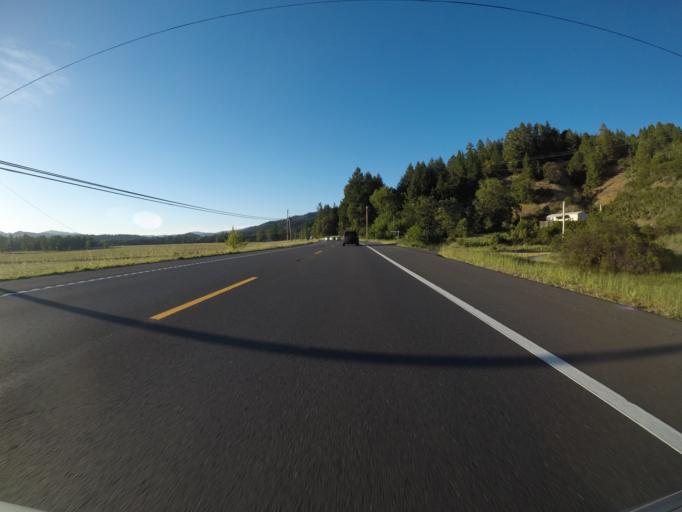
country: US
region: California
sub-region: Mendocino County
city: Laytonville
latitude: 39.6712
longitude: -123.4758
